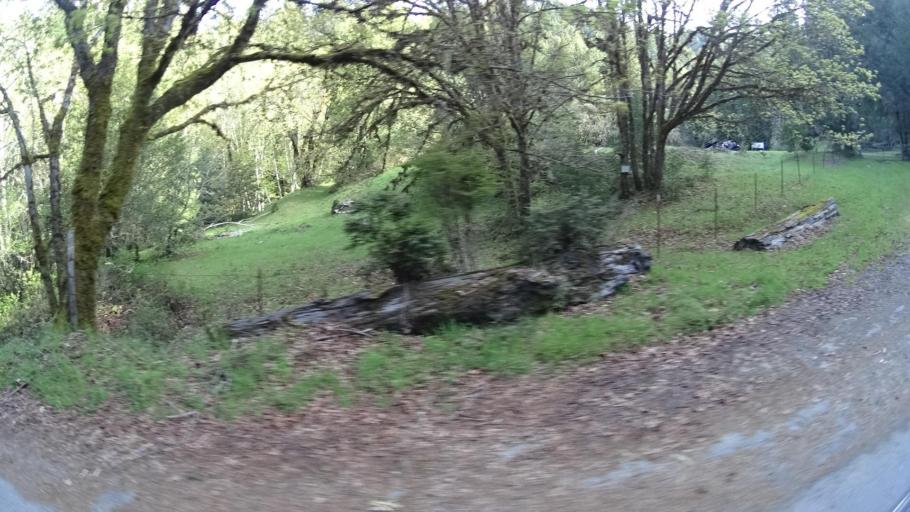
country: US
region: California
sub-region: Humboldt County
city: Blue Lake
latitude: 40.6976
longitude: -123.9369
